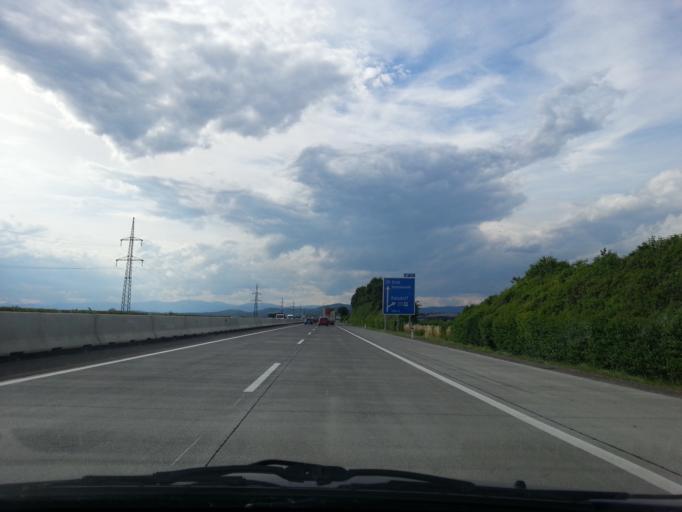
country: AT
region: Styria
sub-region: Politischer Bezirk Graz-Umgebung
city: Wundschuh
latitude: 46.9528
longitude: 15.4464
